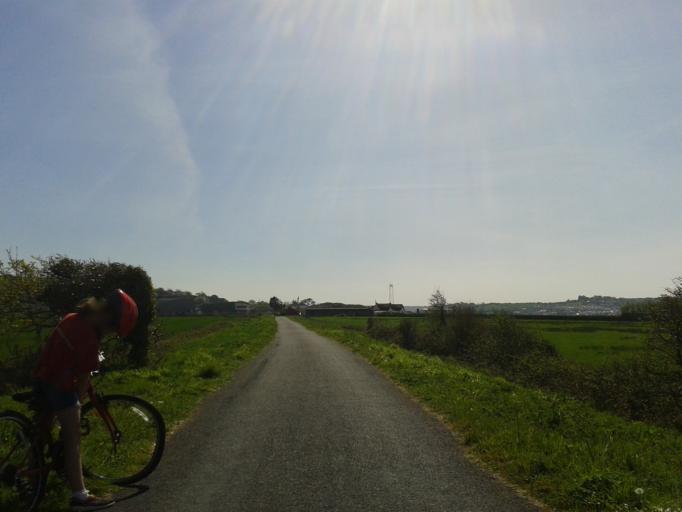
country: GB
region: England
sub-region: Devon
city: Appledore
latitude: 51.0634
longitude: -4.1752
